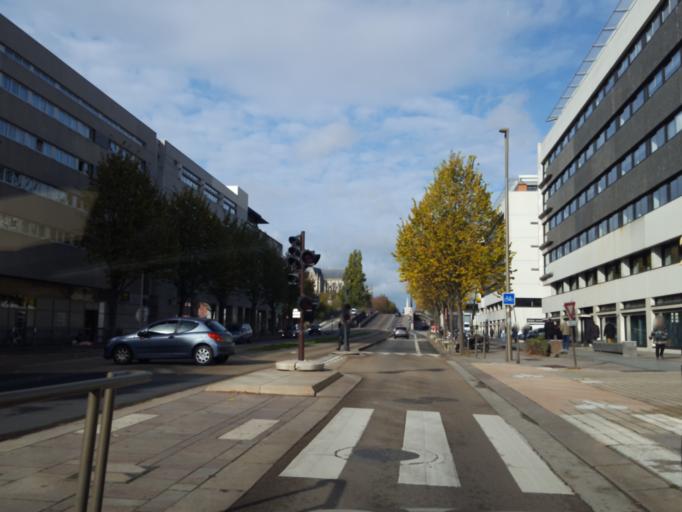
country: FR
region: Pays de la Loire
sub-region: Departement de la Loire-Atlantique
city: Nantes
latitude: 47.2138
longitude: -1.5450
